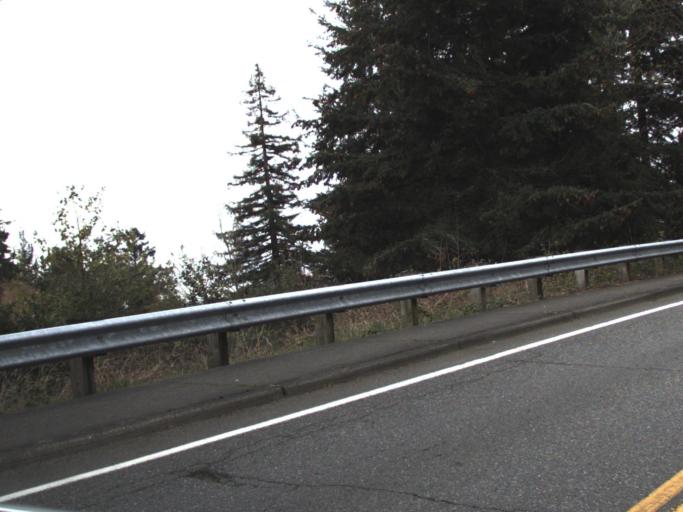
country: US
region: Washington
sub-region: King County
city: Des Moines
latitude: 47.4081
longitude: -122.3308
